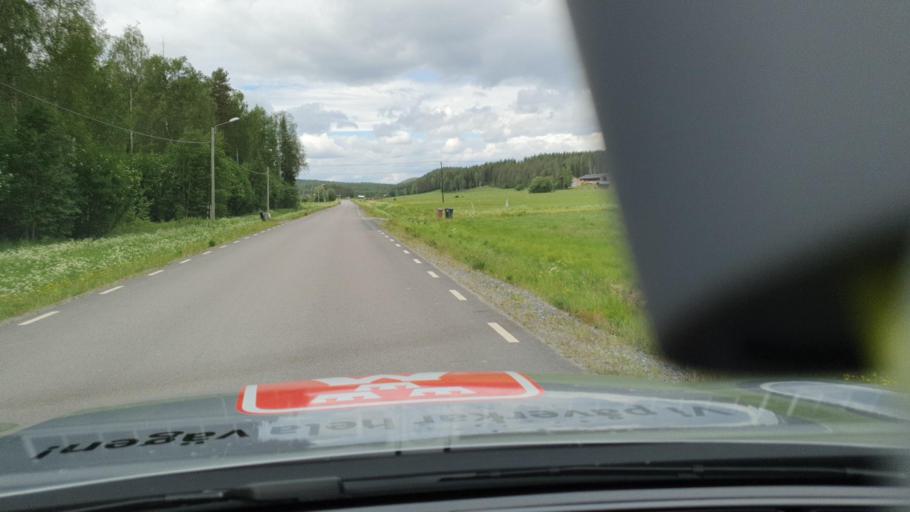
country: SE
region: Norrbotten
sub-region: Lulea Kommun
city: Sodra Sunderbyn
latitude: 65.8580
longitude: 21.9184
